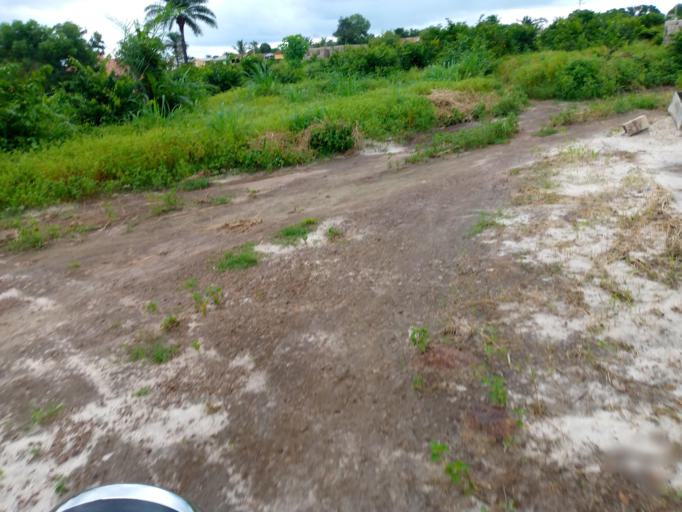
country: SL
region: Southern Province
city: Moyamba
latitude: 8.1536
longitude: -12.4392
